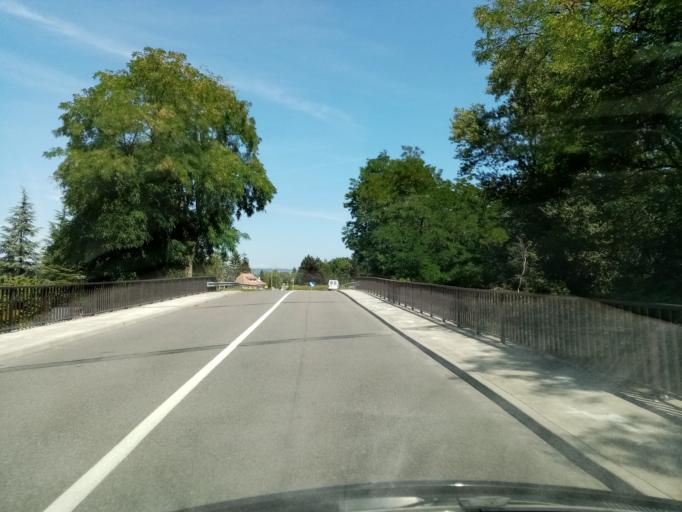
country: FR
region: Alsace
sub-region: Departement du Haut-Rhin
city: Neuf-Brisach
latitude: 48.0227
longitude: 7.5327
